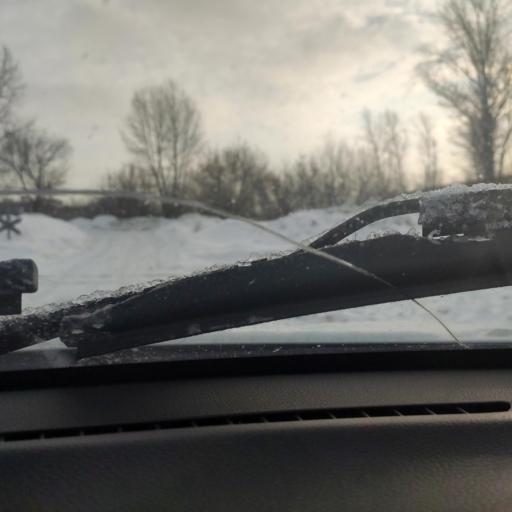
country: RU
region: Tatarstan
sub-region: Gorod Kazan'
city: Kazan
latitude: 55.8433
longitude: 49.0718
